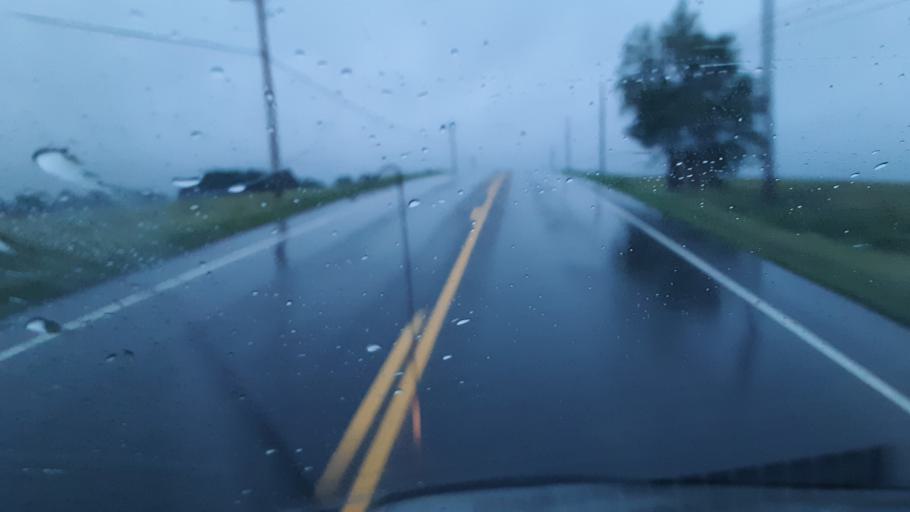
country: US
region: Maine
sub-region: Penobscot County
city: Patten
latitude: 45.9552
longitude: -68.4522
